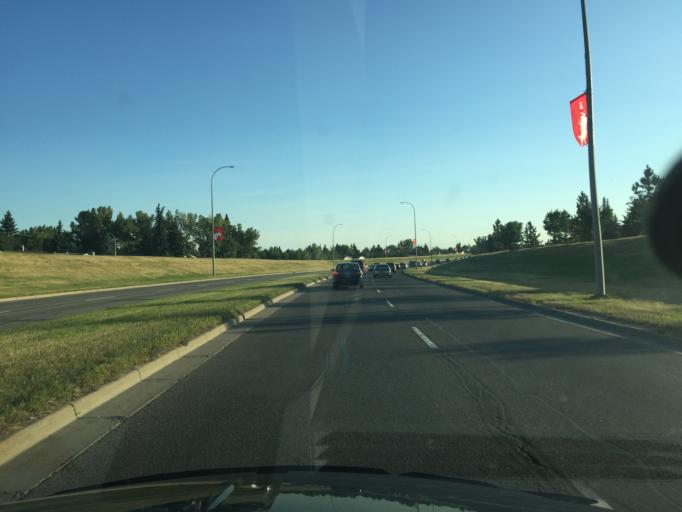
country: CA
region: Alberta
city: Calgary
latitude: 50.9357
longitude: -114.0329
